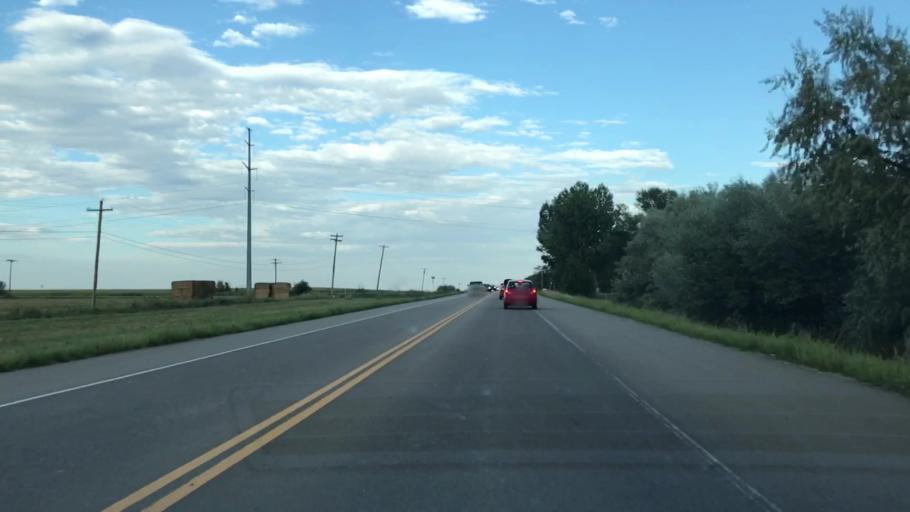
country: US
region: Colorado
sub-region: Weld County
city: Mead
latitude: 40.2038
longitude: -105.0385
